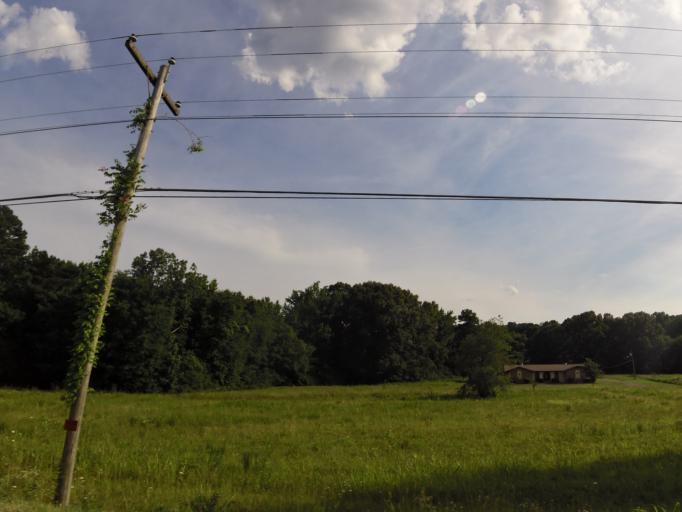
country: US
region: Tennessee
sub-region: Benton County
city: Camden
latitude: 36.0151
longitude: -88.0528
